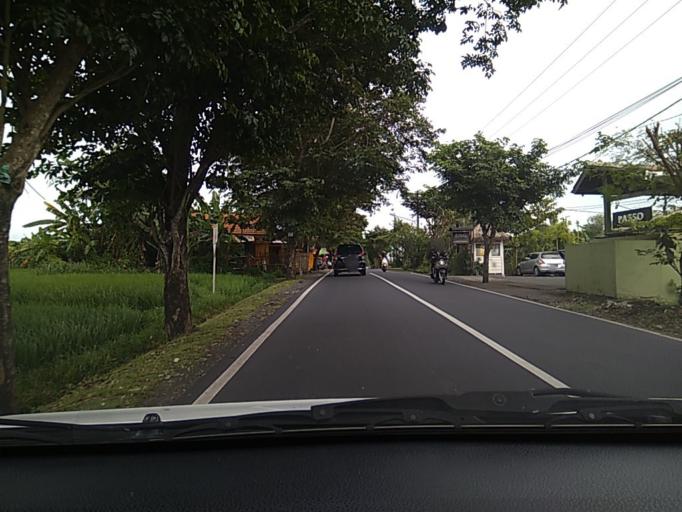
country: ID
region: Bali
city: Banjar Kerobokan
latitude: -8.6283
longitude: 115.1294
